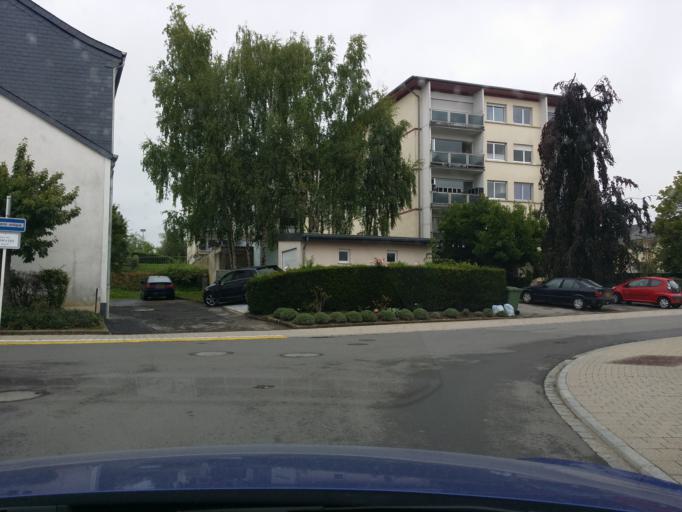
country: LU
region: Luxembourg
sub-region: Canton de Luxembourg
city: Strassen
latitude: 49.6188
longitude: 6.0694
